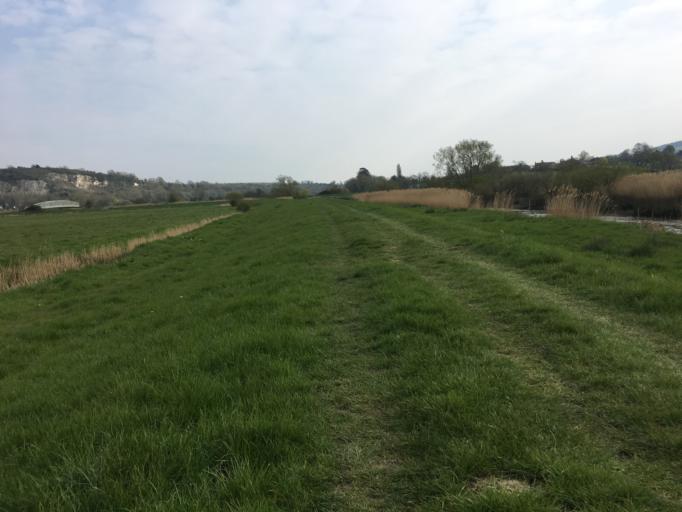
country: GB
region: England
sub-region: West Sussex
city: Arundel
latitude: 50.9009
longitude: -0.5522
